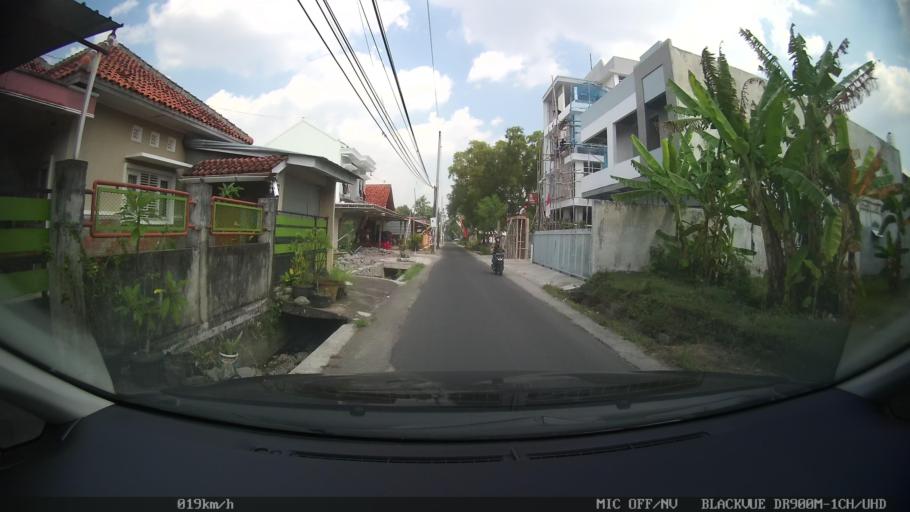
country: ID
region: Daerah Istimewa Yogyakarta
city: Depok
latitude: -7.7944
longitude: 110.4058
